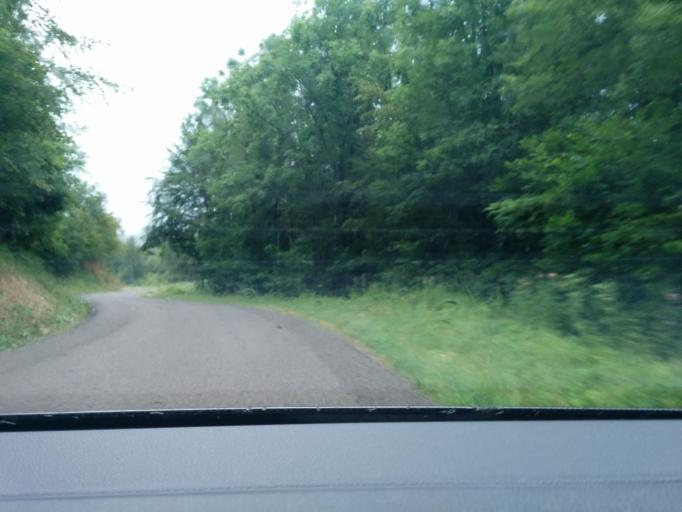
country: FR
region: Franche-Comte
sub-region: Departement du Jura
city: Saint-Lupicin
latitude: 46.4312
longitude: 5.8116
